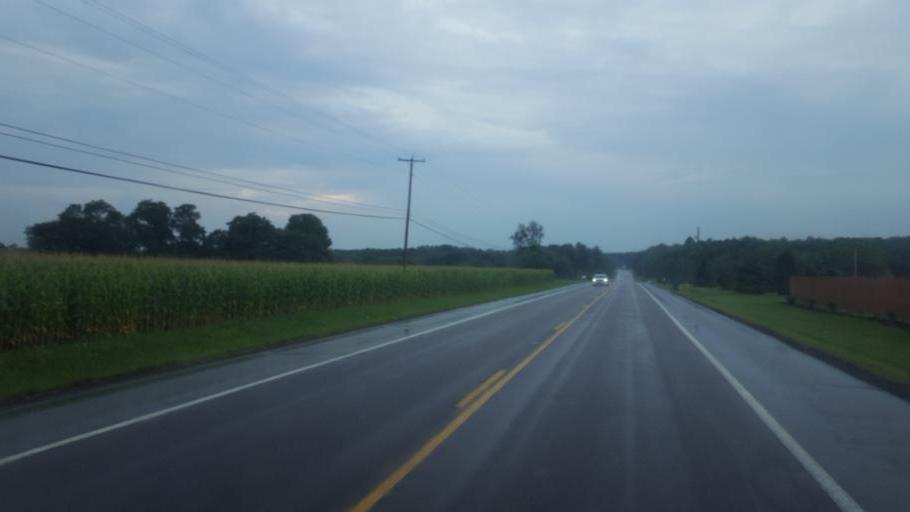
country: US
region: Ohio
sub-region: Geauga County
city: Middlefield
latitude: 41.3825
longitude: -81.0628
